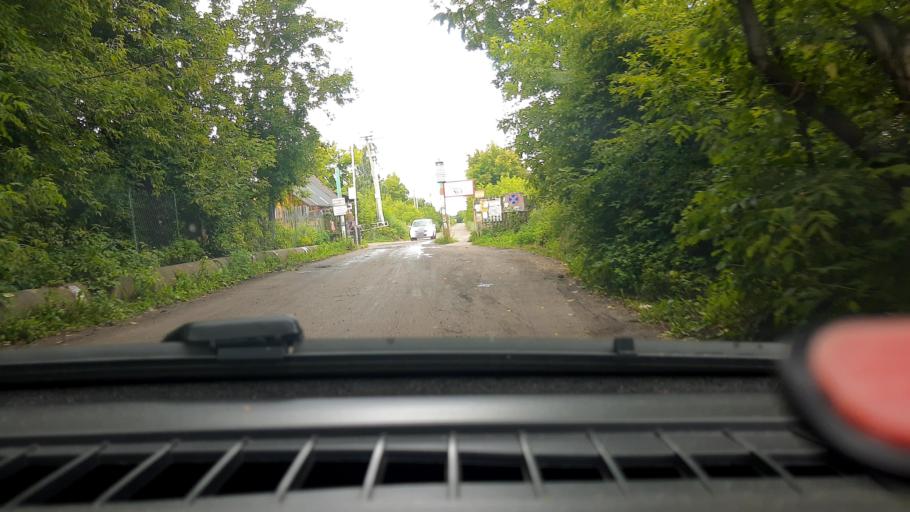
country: RU
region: Nizjnij Novgorod
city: Gorbatovka
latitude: 56.2566
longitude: 43.8305
